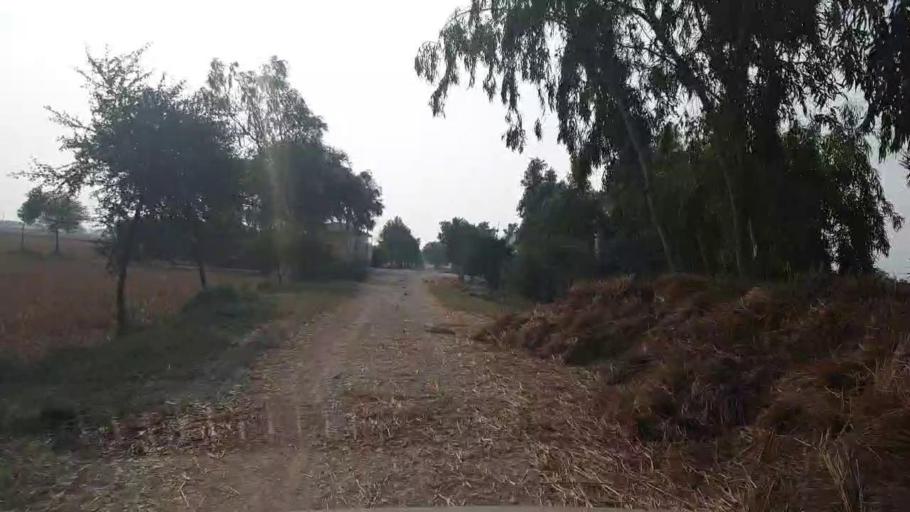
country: PK
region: Sindh
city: Tando Muhammad Khan
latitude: 25.0956
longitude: 68.5039
